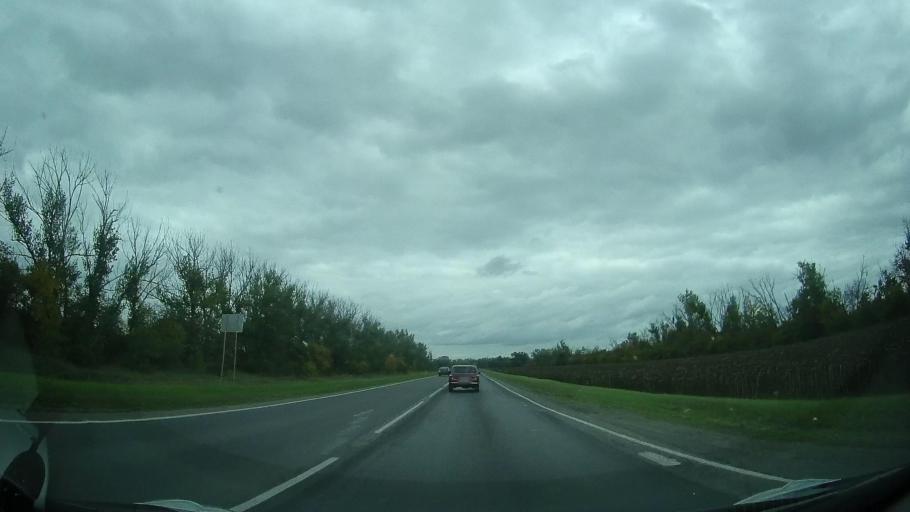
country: RU
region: Rostov
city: Yegorlykskaya
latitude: 46.5399
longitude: 40.7757
